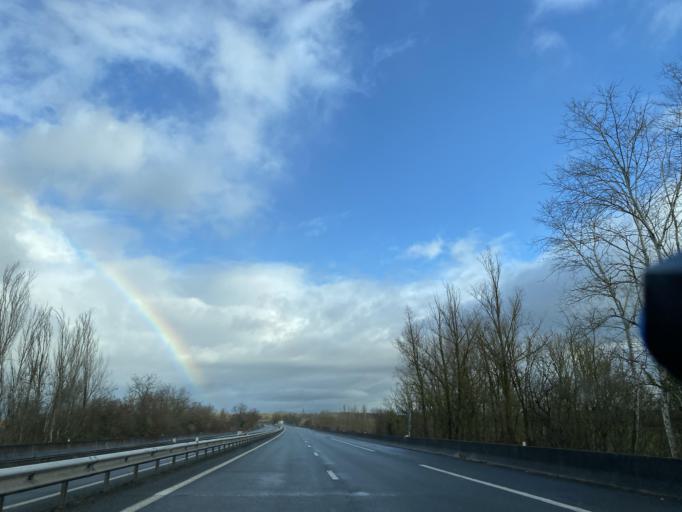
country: FR
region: Centre
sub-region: Departement du Cher
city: Orval
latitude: 46.7801
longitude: 2.4091
